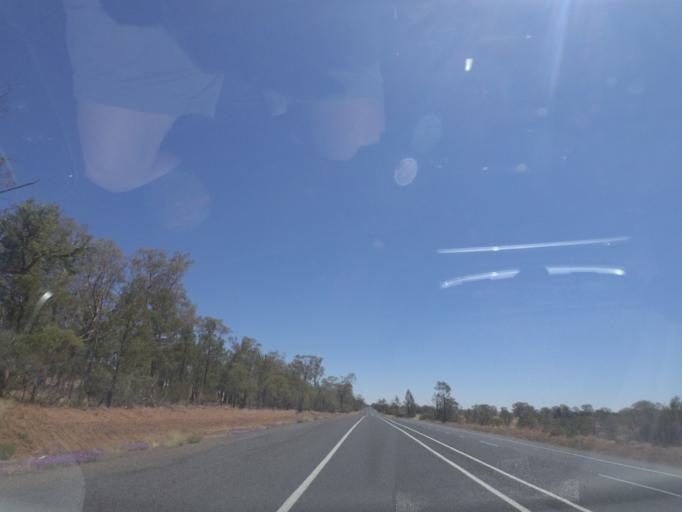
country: AU
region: New South Wales
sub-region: Gilgandra
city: Gilgandra
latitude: -31.4951
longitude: 148.8652
